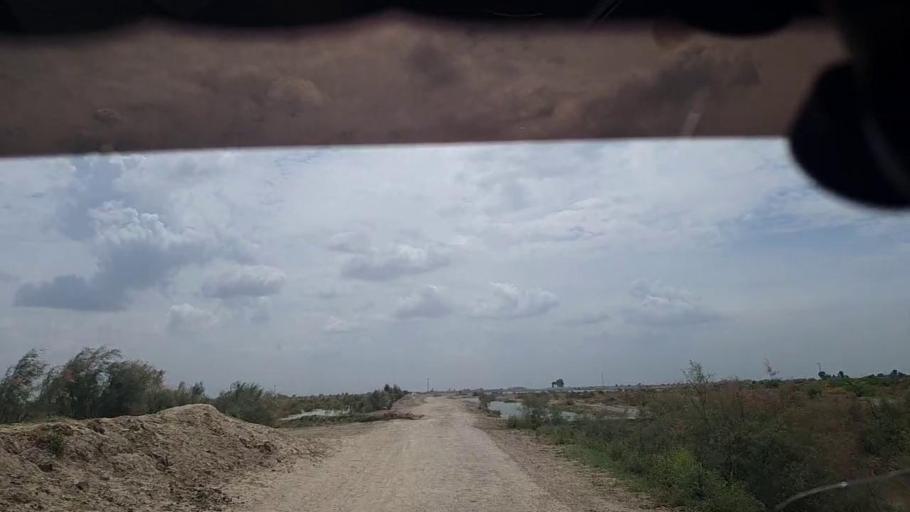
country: PK
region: Sindh
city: Rustam jo Goth
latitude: 28.0311
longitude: 68.9359
